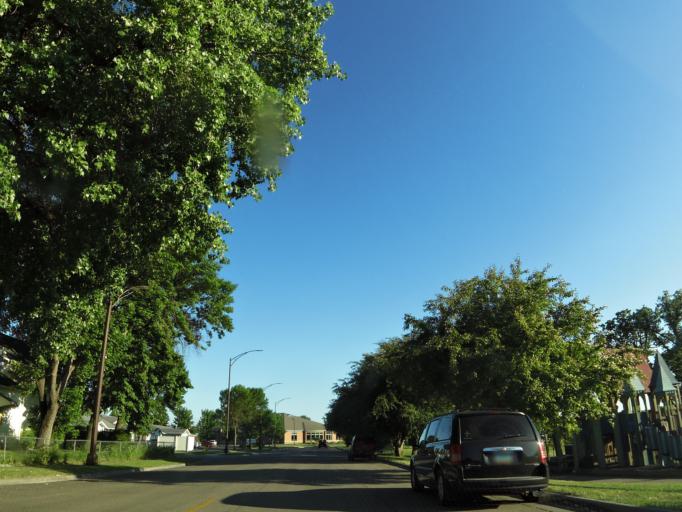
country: US
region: Minnesota
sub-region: Polk County
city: East Grand Forks
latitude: 47.9325
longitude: -97.0256
